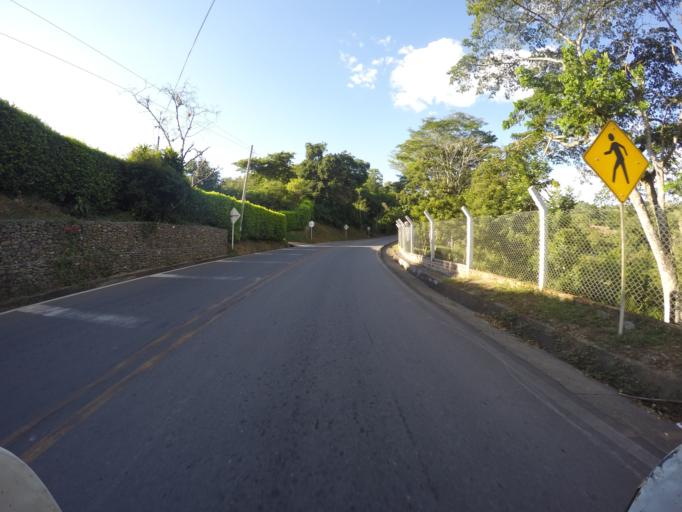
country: CO
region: Valle del Cauca
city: Alcala
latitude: 4.7032
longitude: -75.8492
